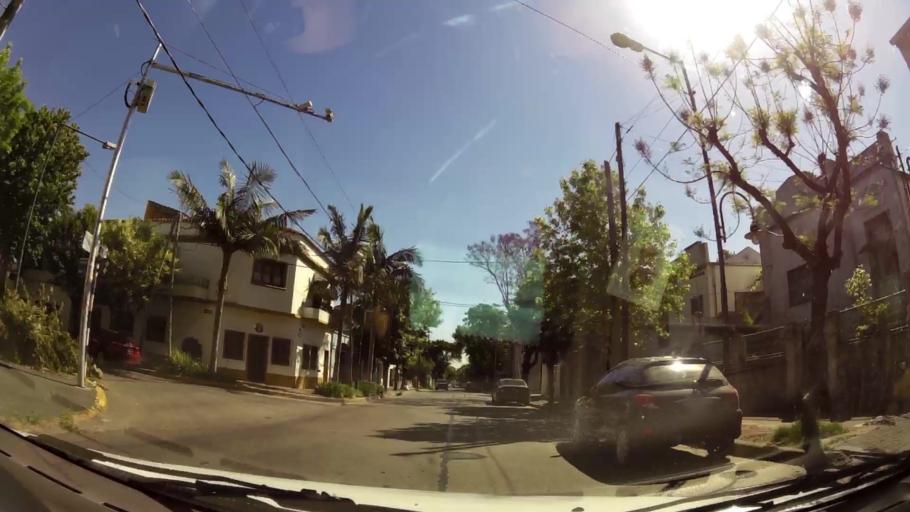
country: AR
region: Buenos Aires
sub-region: Partido de San Isidro
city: San Isidro
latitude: -34.4545
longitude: -58.5316
